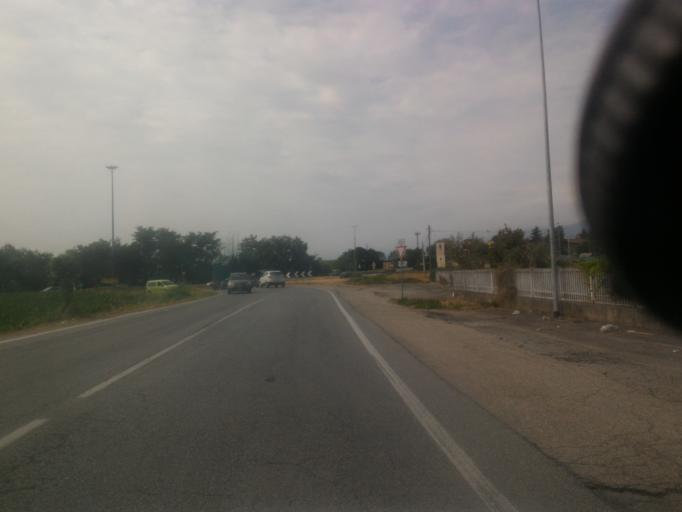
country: IT
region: Piedmont
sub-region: Provincia di Torino
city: Bricherasio
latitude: 44.8264
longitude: 7.3121
